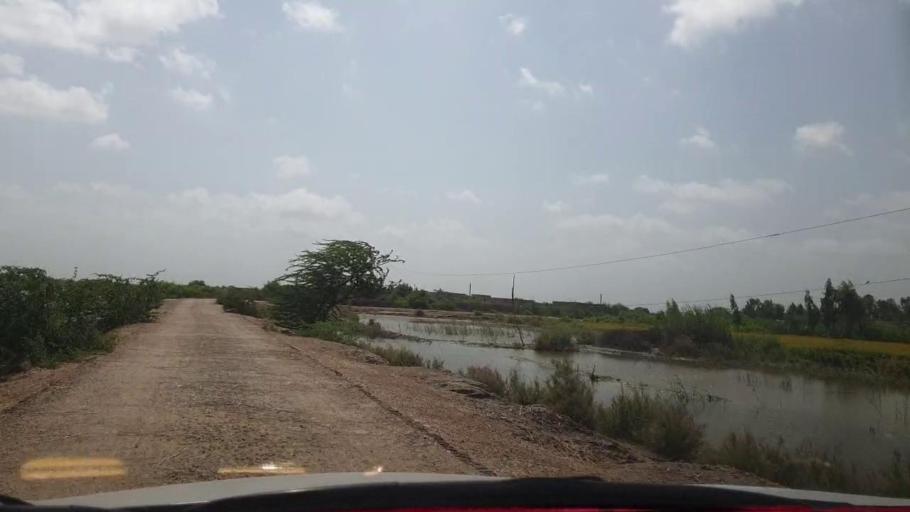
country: PK
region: Sindh
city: Talhar
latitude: 24.9027
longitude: 68.8596
